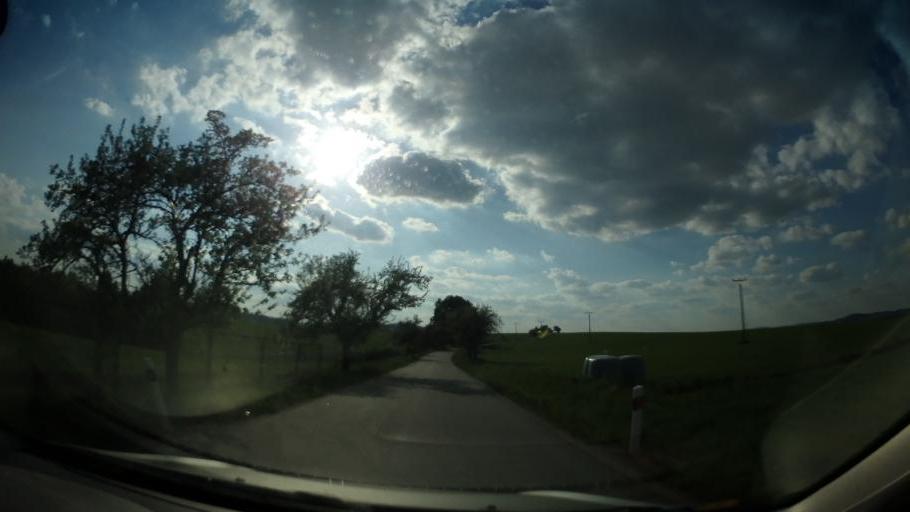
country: CZ
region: Vysocina
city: Merin
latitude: 49.3517
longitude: 15.9293
